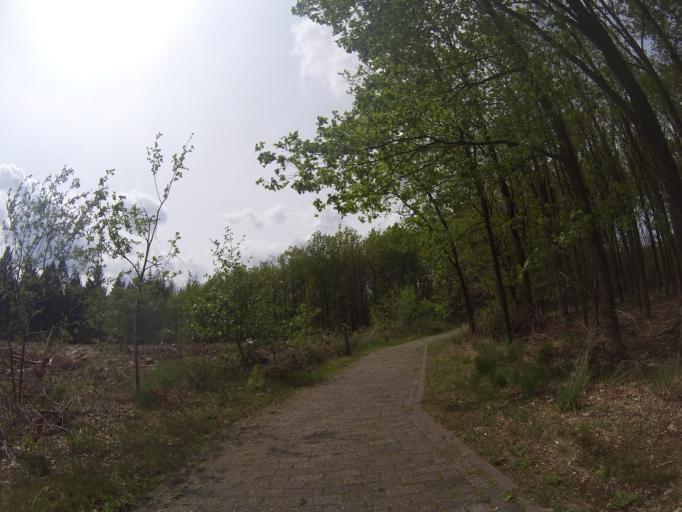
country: NL
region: Drenthe
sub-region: Gemeente Assen
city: Assen
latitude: 52.9184
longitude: 6.5955
